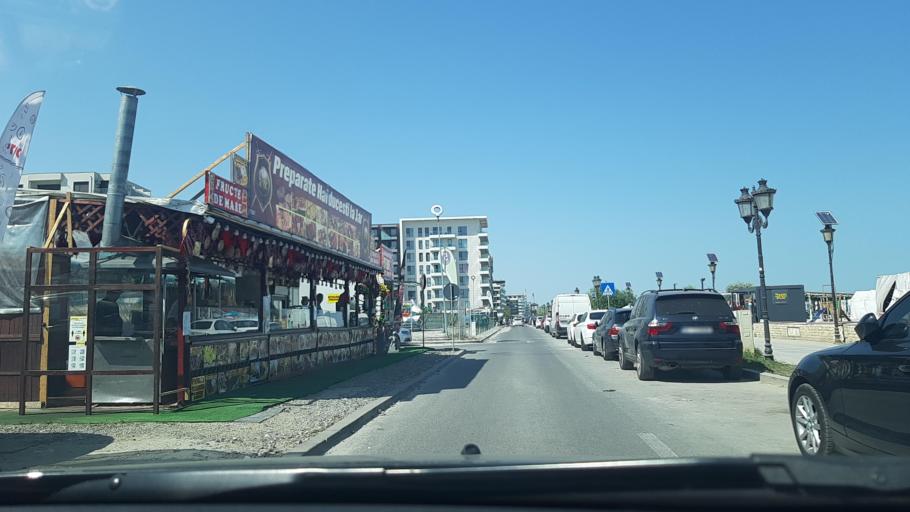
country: RO
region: Constanta
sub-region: Comuna Navodari
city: Navodari
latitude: 44.3032
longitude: 28.6272
